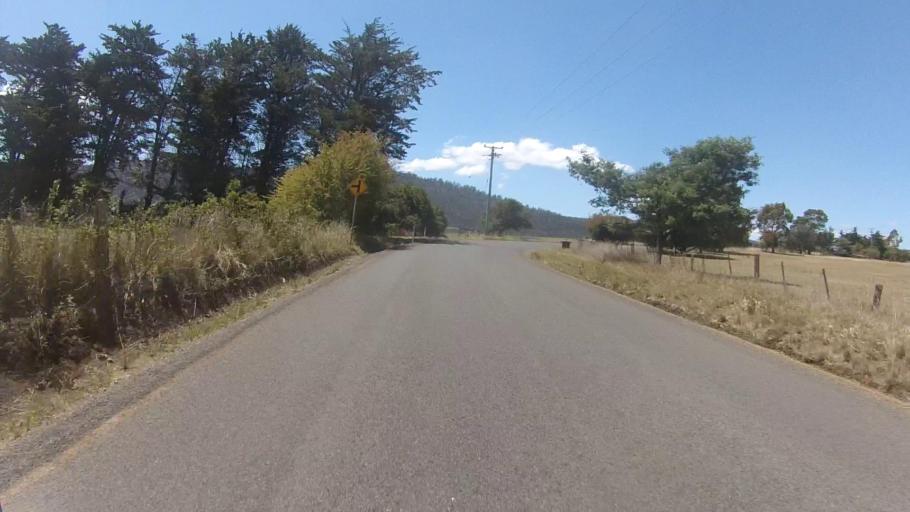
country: AU
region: Tasmania
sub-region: Sorell
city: Sorell
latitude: -42.7607
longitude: 147.6204
